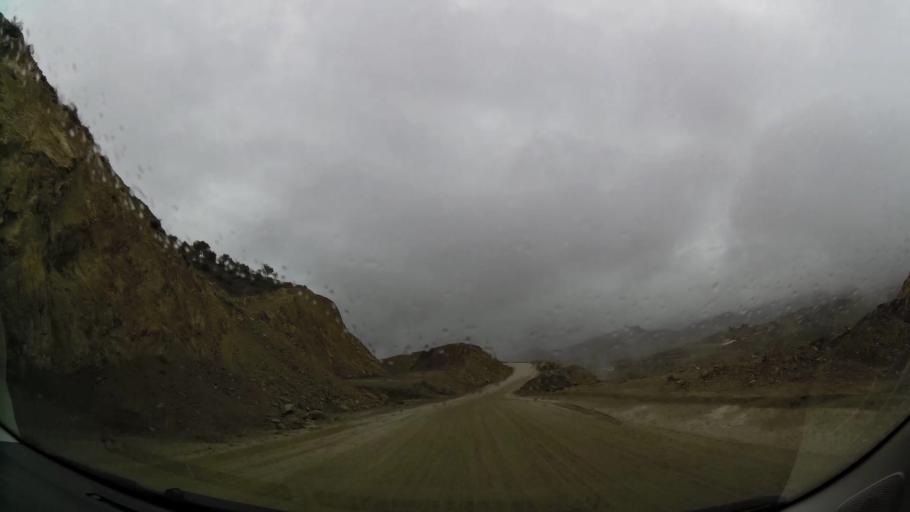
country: MA
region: Oriental
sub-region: Nador
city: Midar
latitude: 34.8979
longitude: -3.7786
